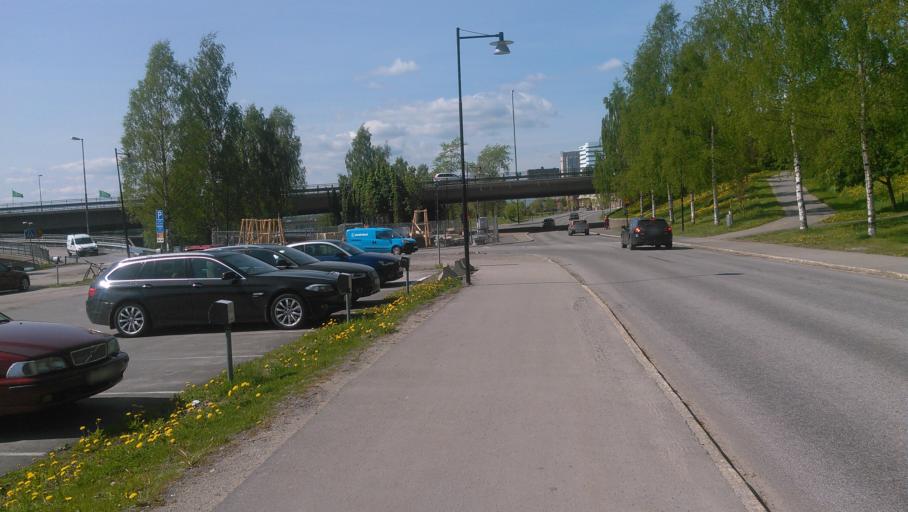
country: SE
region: Vaesterbotten
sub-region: Umea Kommun
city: Umea
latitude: 63.8221
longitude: 20.2708
